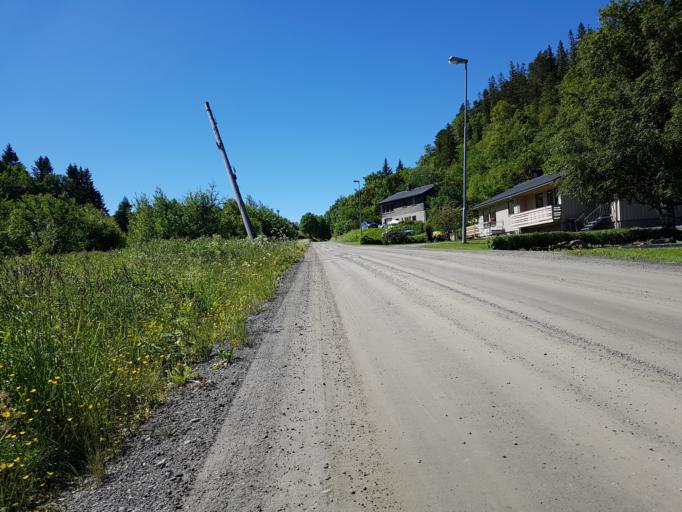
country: NO
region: Sor-Trondelag
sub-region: Skaun
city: Borsa
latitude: 63.4349
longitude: 10.1870
